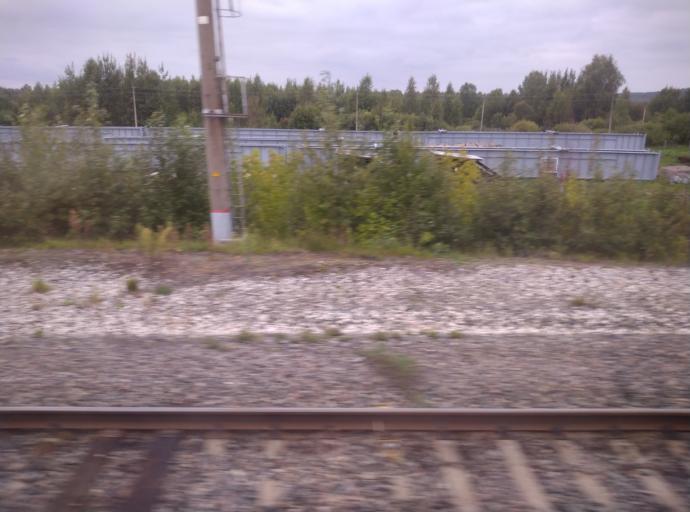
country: RU
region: Kostroma
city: Kosmynino
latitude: 57.5926
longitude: 40.7687
